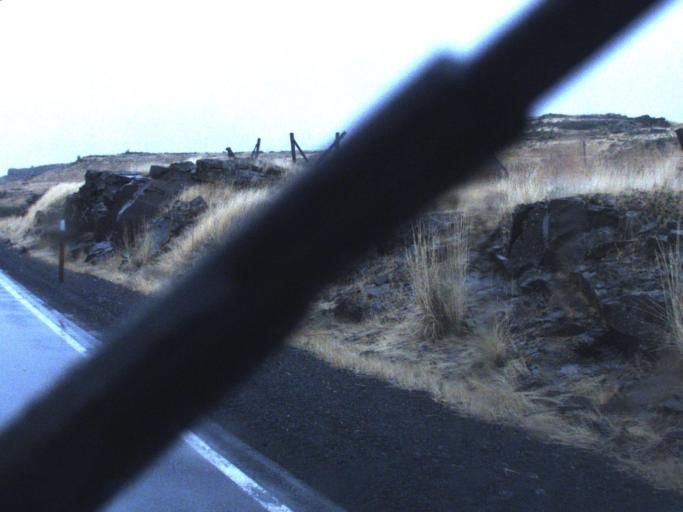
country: US
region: Washington
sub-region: Spokane County
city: Medical Lake
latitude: 47.2472
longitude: -117.9213
